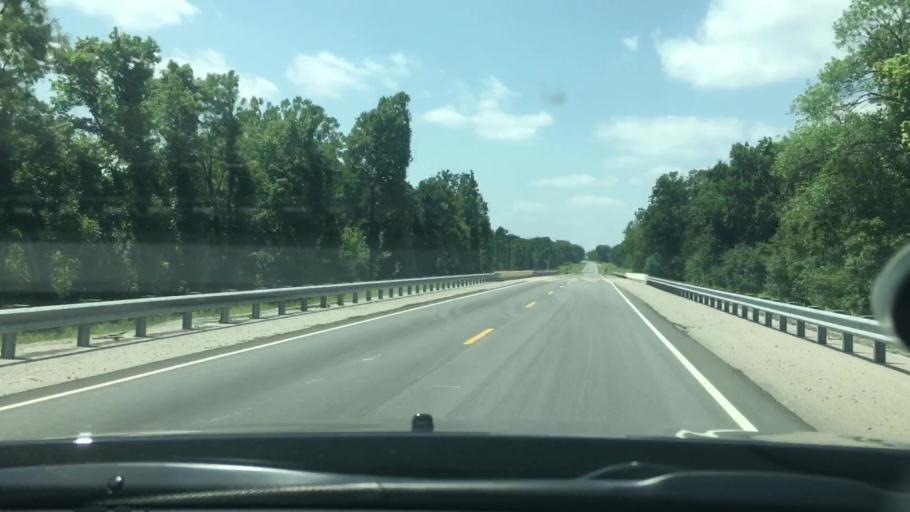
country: US
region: Oklahoma
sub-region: Atoka County
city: Atoka
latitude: 34.3791
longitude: -96.2781
